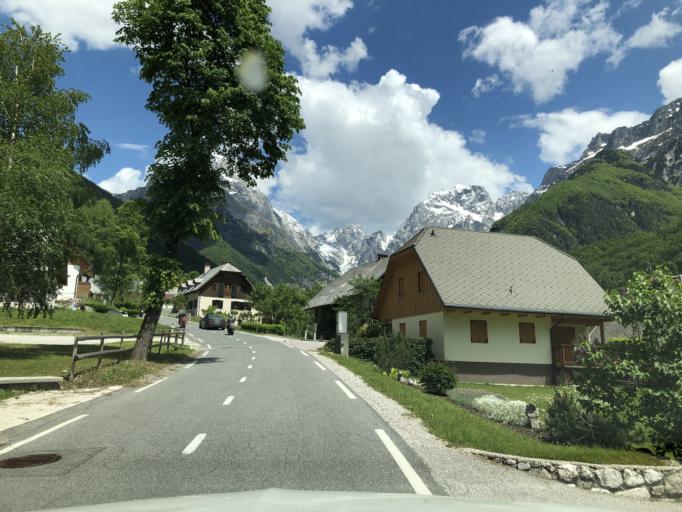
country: SI
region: Bovec
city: Bovec
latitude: 46.4049
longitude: 13.6018
